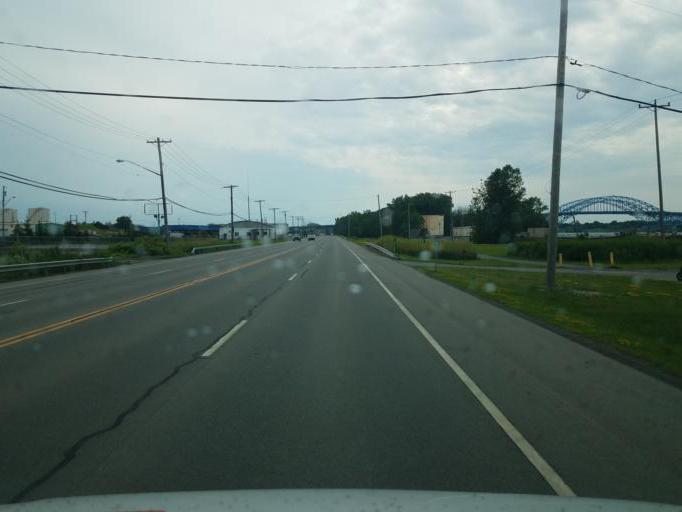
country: US
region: New York
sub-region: Erie County
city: Grandyle Village
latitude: 43.0012
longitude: -78.9261
